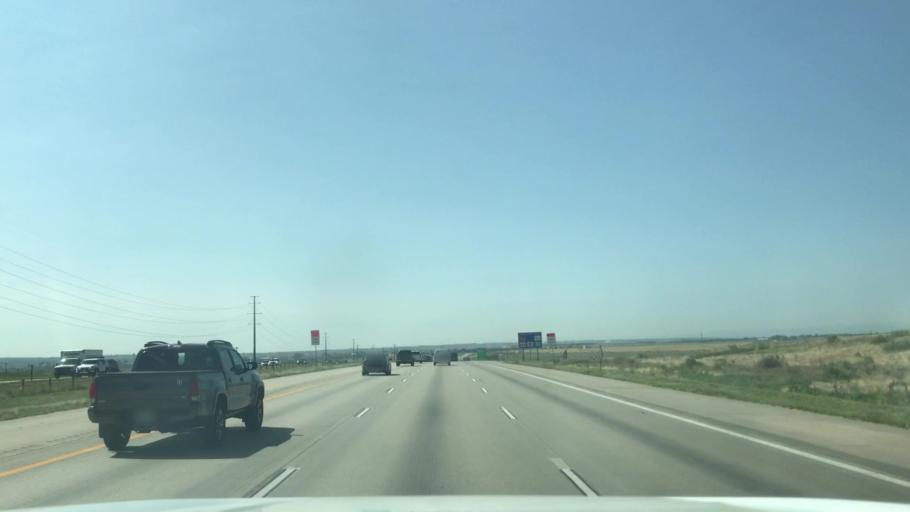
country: US
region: Colorado
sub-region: Boulder County
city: Erie
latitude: 40.0185
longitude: -104.9809
